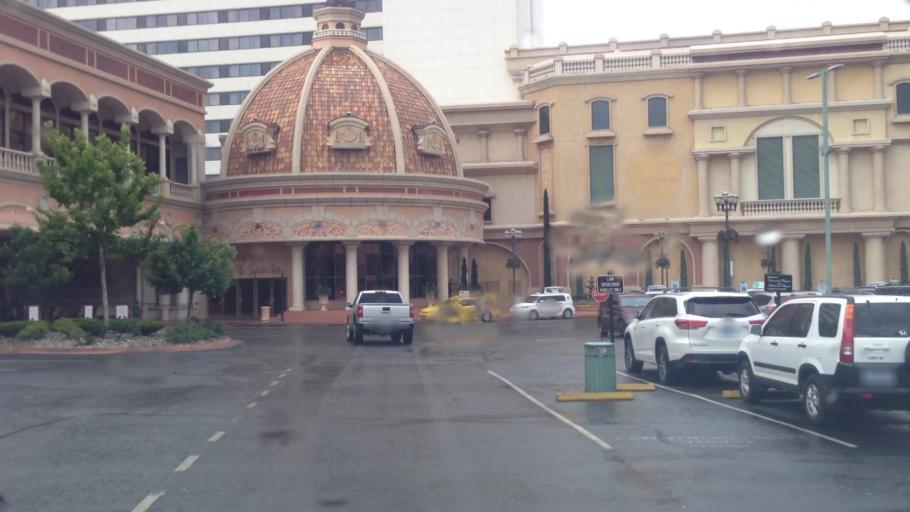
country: US
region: Nevada
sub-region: Washoe County
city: Reno
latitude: 39.4968
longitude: -119.8000
